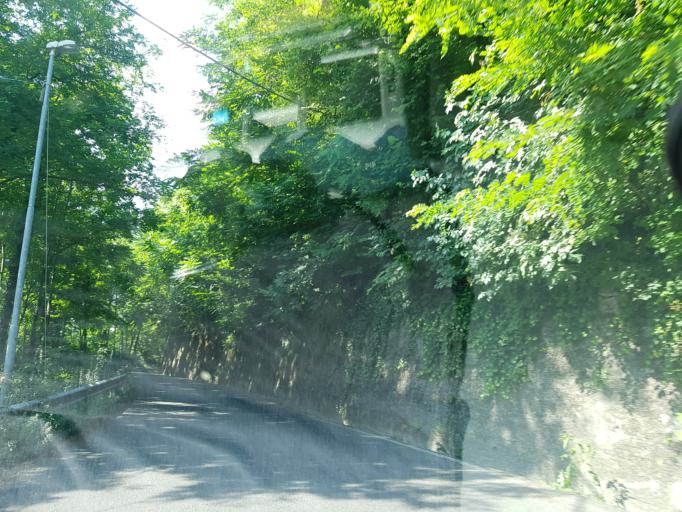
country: IT
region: Liguria
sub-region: Provincia di Genova
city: Pedemonte
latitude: 44.5014
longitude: 8.9159
